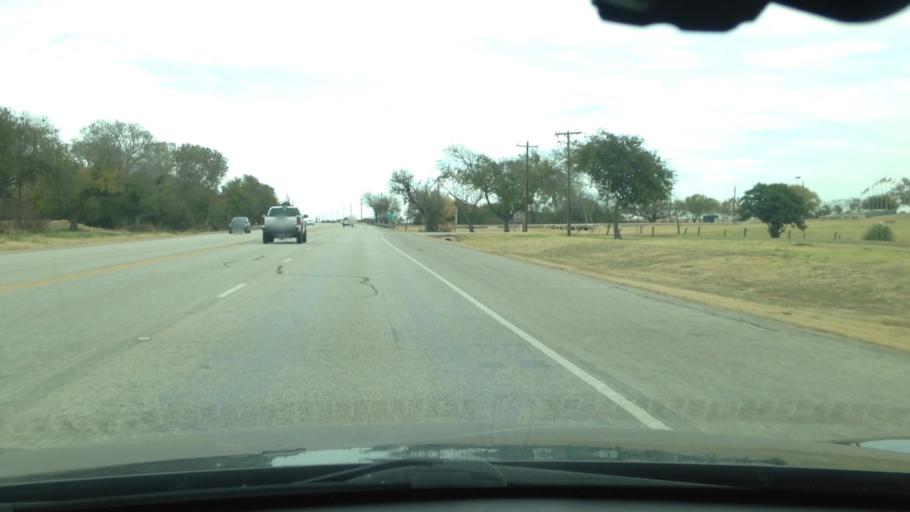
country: US
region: Texas
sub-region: Hays County
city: San Marcos
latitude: 29.8843
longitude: -97.8930
